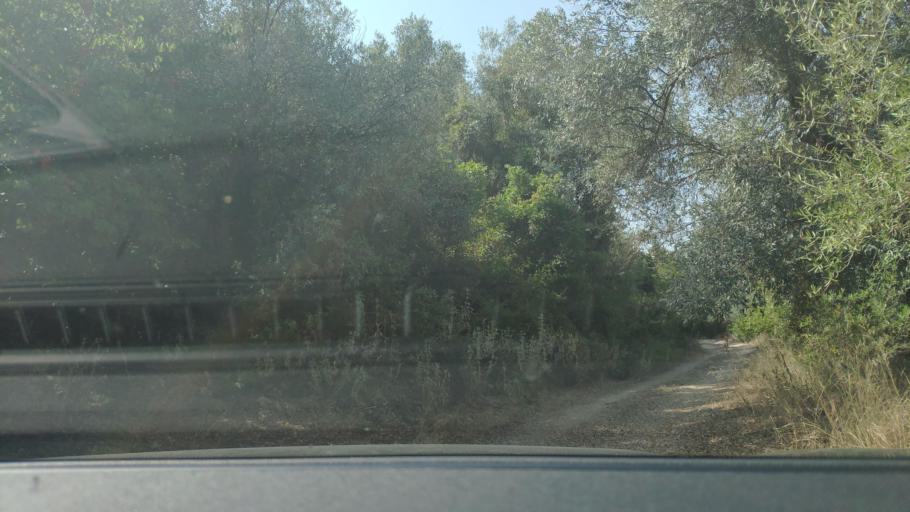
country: GR
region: West Greece
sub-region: Nomos Aitolias kai Akarnanias
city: Fitiai
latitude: 38.7326
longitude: 21.1830
